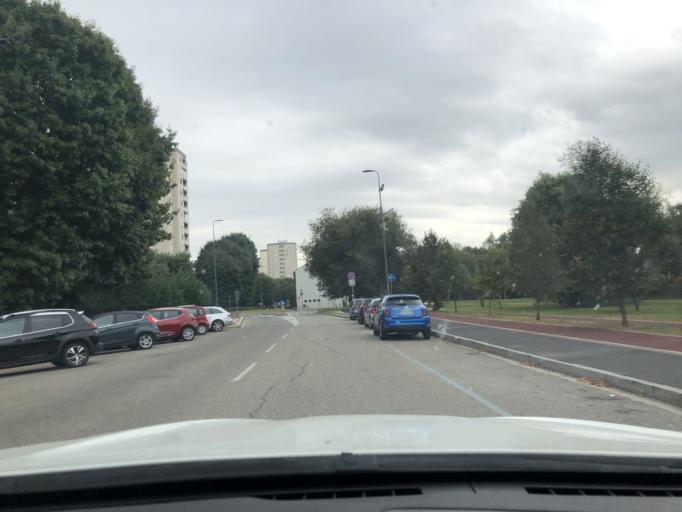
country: IT
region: Lombardy
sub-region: Citta metropolitana di Milano
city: Pero
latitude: 45.5032
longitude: 9.0991
